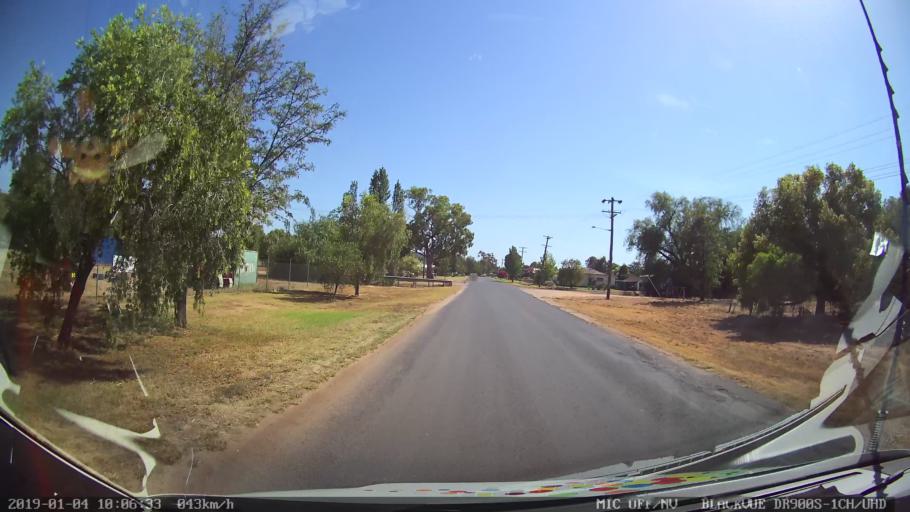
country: AU
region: New South Wales
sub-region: Cabonne
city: Canowindra
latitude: -33.4332
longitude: 148.3689
